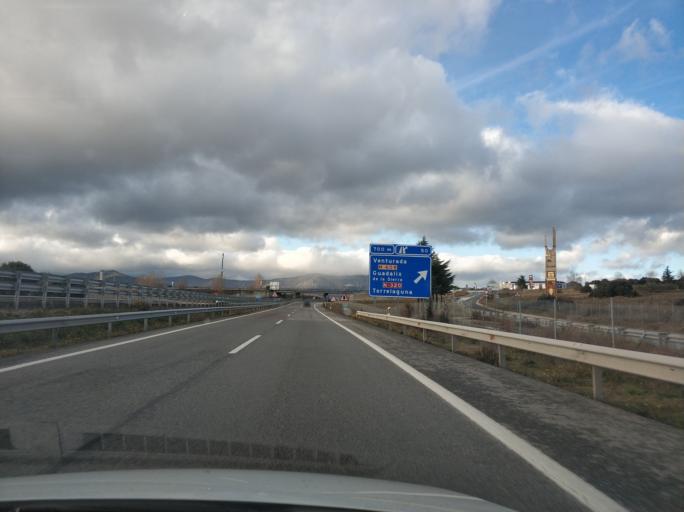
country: ES
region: Madrid
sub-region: Provincia de Madrid
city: Venturada
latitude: 40.7826
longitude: -3.6135
